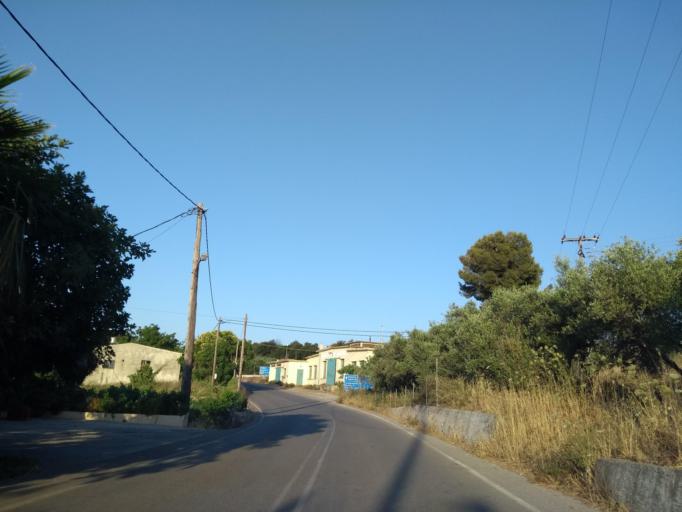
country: GR
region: Crete
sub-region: Nomos Chanias
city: Kalivai
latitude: 35.4074
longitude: 24.2018
